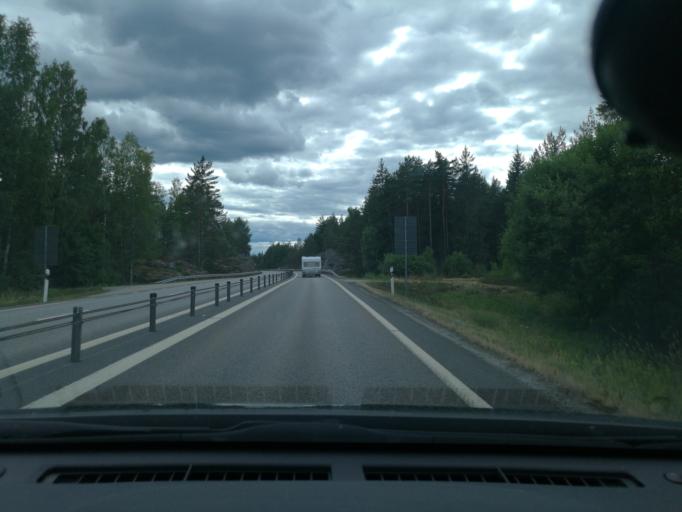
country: SE
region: OEstergoetland
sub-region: Valdemarsviks Kommun
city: Valdemarsvik
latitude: 58.0958
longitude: 16.5297
